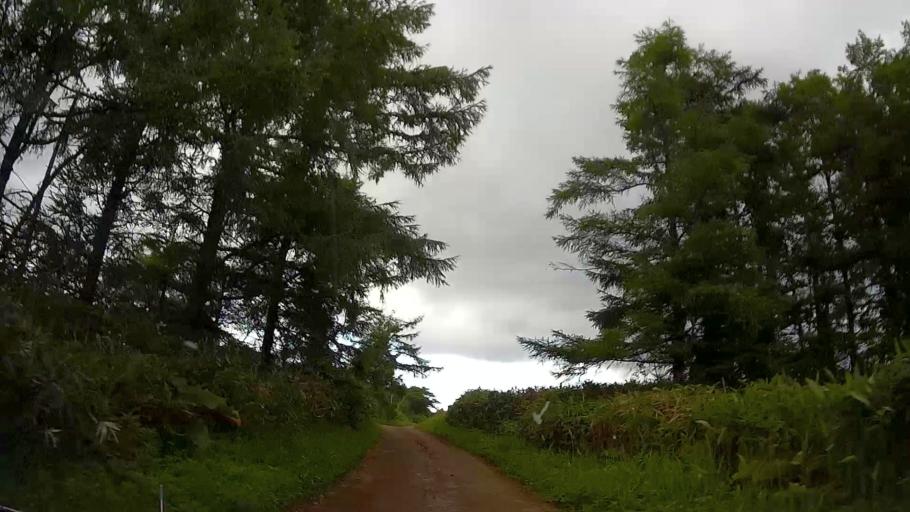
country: JP
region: Hokkaido
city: Nanae
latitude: 42.1236
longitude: 140.4081
